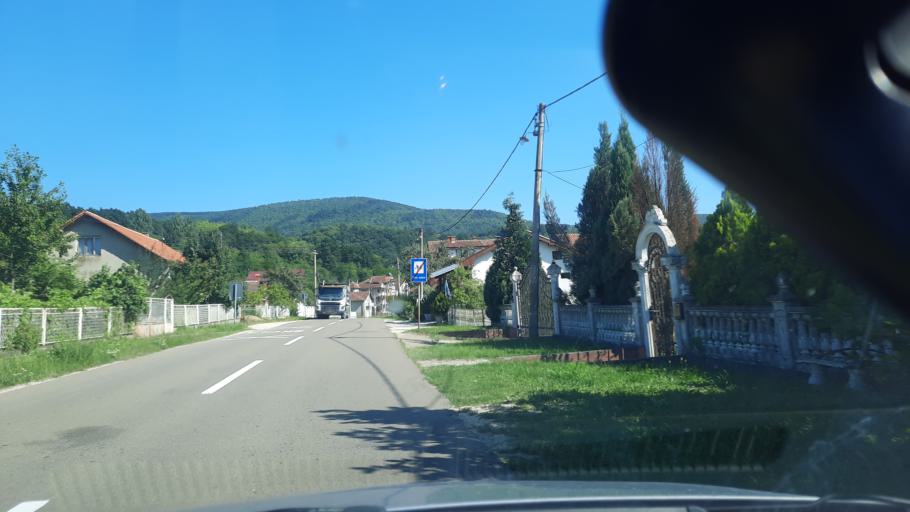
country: RS
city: Turija
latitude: 44.5238
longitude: 21.6386
